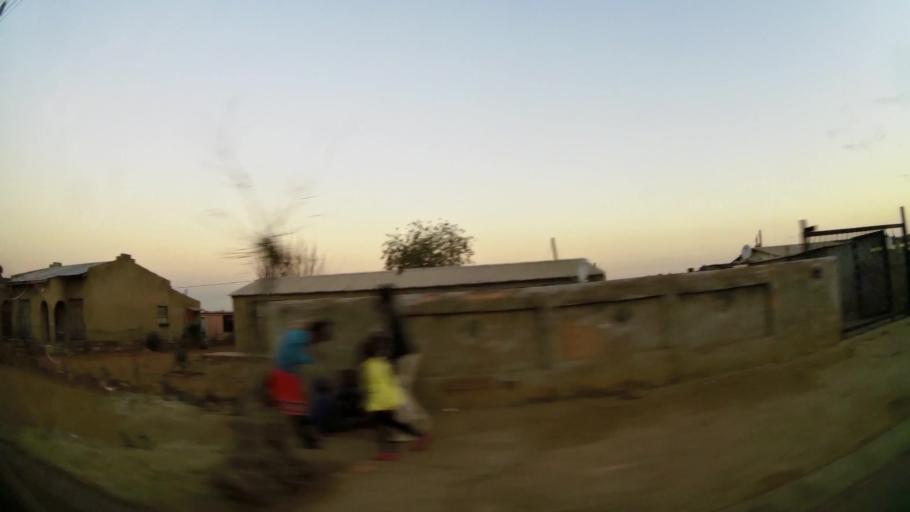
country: ZA
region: Gauteng
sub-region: West Rand District Municipality
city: Randfontein
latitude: -26.2082
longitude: 27.7126
